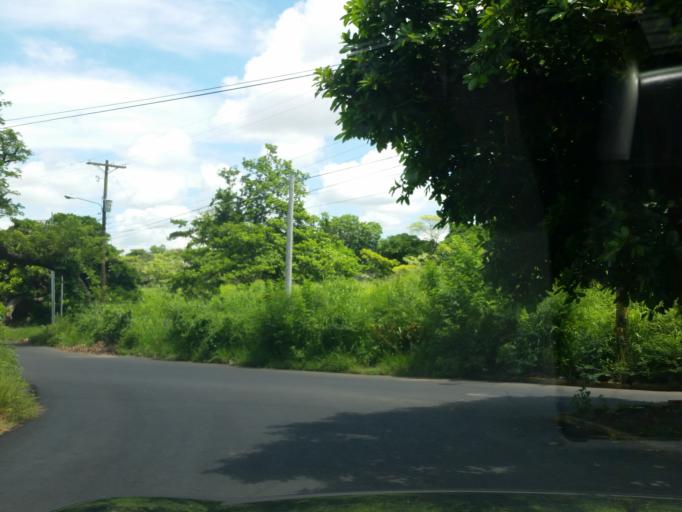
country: NI
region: Managua
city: Managua
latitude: 12.1234
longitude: -86.2681
